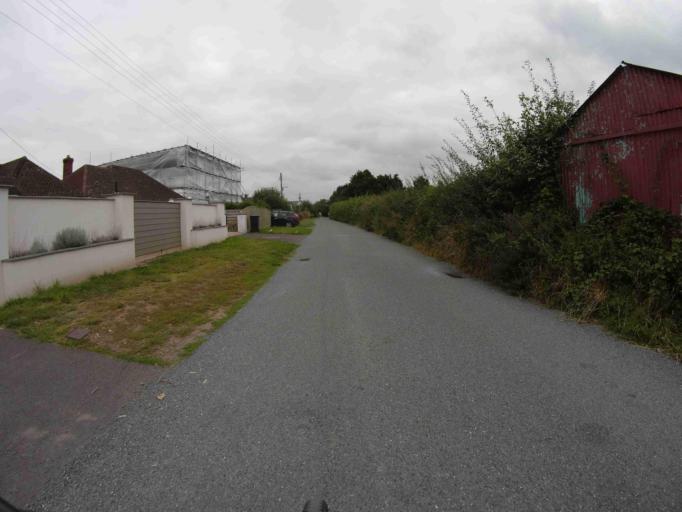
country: GB
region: England
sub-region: Devon
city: Topsham
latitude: 50.6943
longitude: -3.4712
